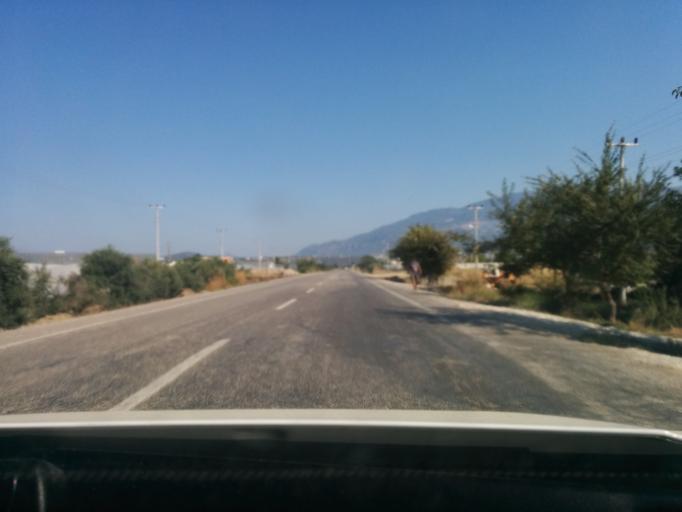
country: TR
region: Antalya
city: Kalkan
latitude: 36.3261
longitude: 29.3317
